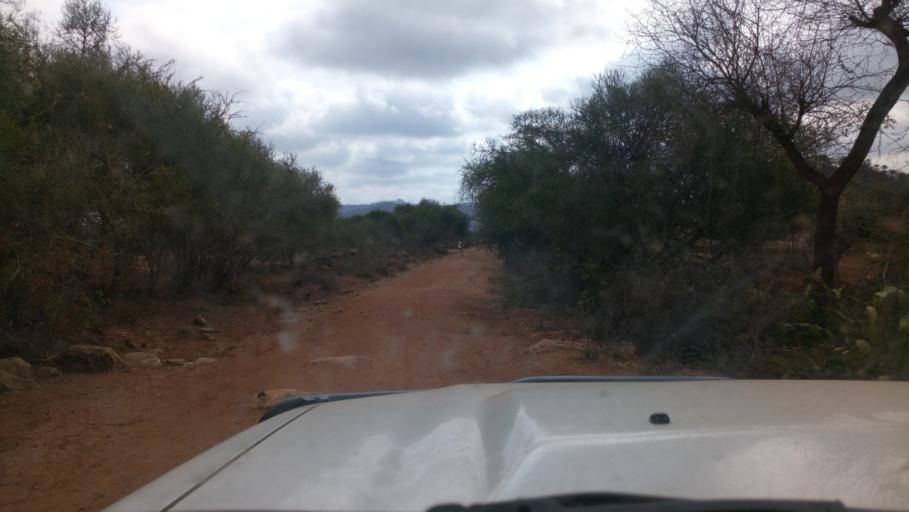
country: KE
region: Kitui
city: Kitui
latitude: -1.8521
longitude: 38.2503
